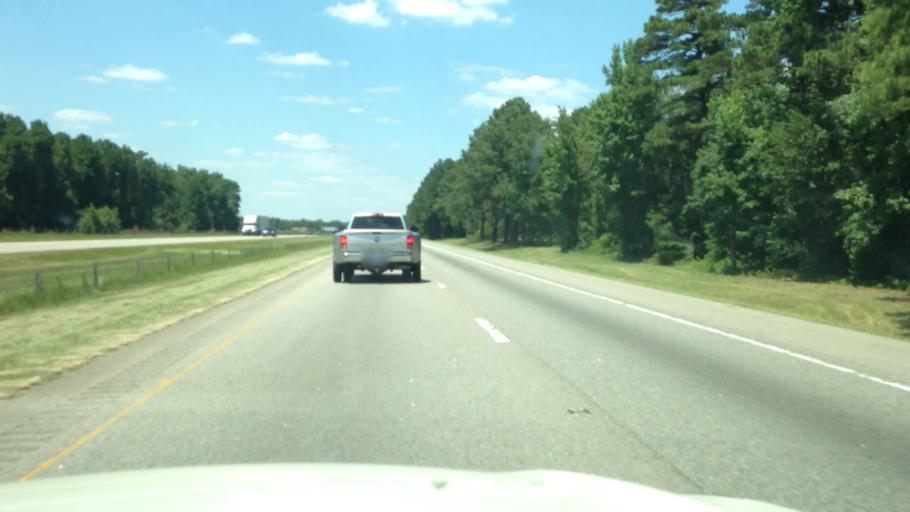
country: US
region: North Carolina
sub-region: Robeson County
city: Saint Pauls
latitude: 34.7851
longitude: -78.9948
